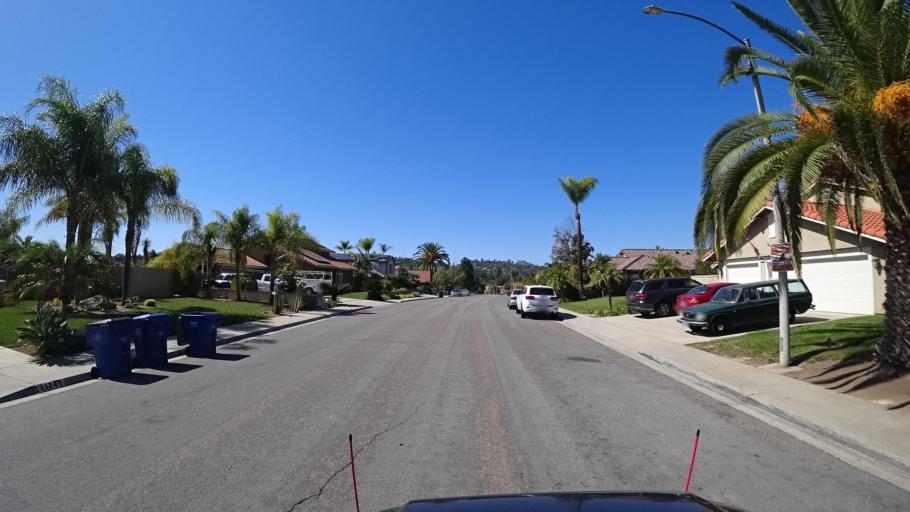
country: US
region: California
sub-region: San Diego County
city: Rancho San Diego
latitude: 32.7579
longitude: -116.9388
